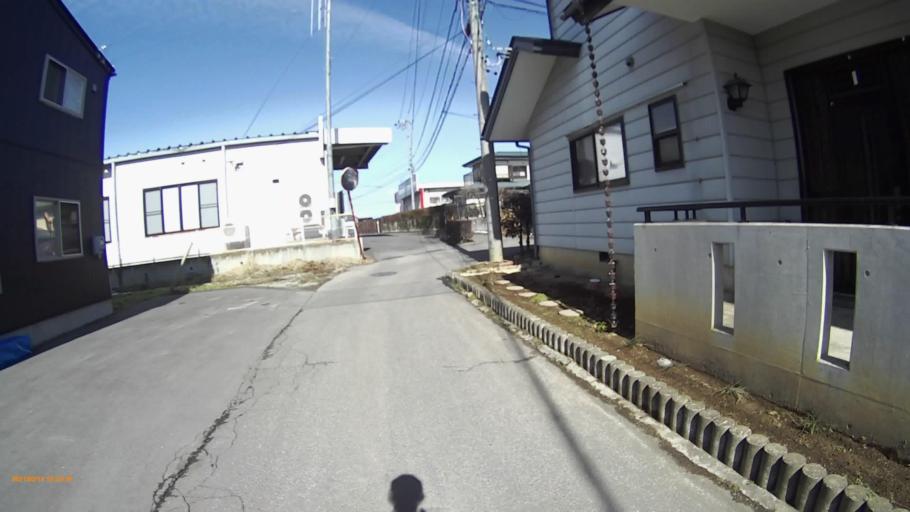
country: JP
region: Nagano
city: Nakano
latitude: 36.7537
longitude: 138.3556
